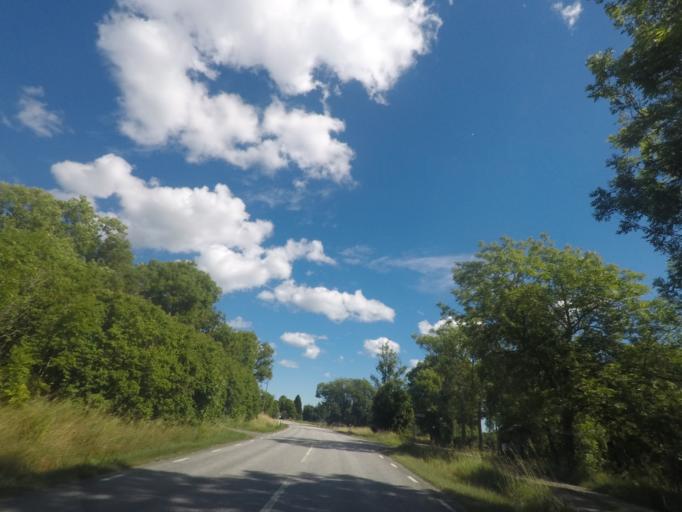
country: SE
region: Stockholm
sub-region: Norrtalje Kommun
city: Hallstavik
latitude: 59.9572
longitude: 18.7914
